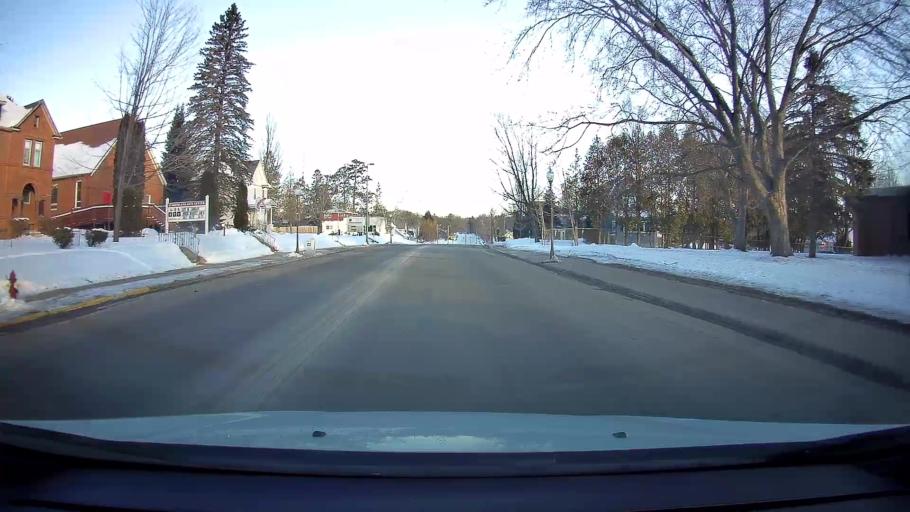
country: US
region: Wisconsin
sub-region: Barron County
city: Cumberland
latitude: 45.5385
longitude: -92.0219
